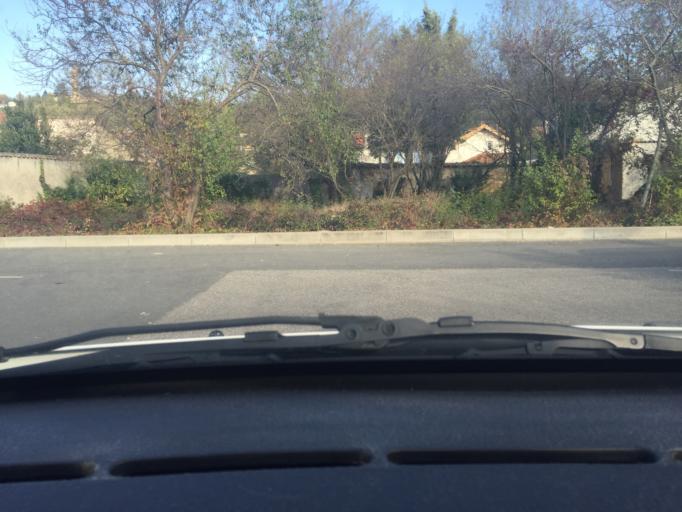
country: FR
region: Rhone-Alpes
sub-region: Departement de l'Ain
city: Miribel
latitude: 45.8248
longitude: 4.9574
